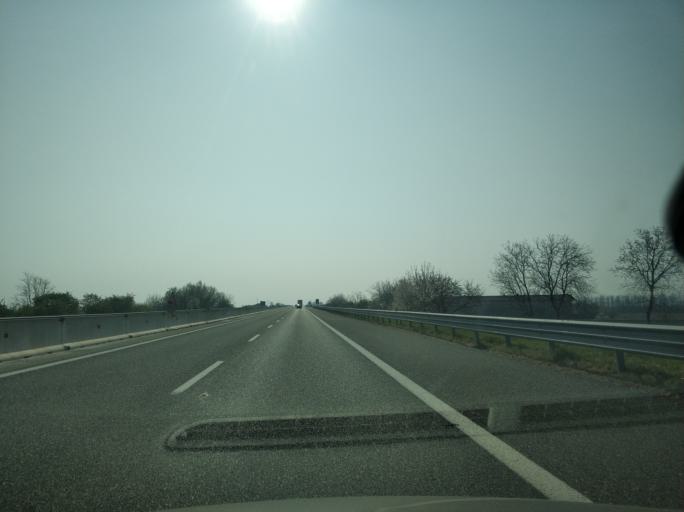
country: IT
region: Piedmont
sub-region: Provincia di Vercelli
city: Santhia
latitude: 45.3636
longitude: 8.1518
